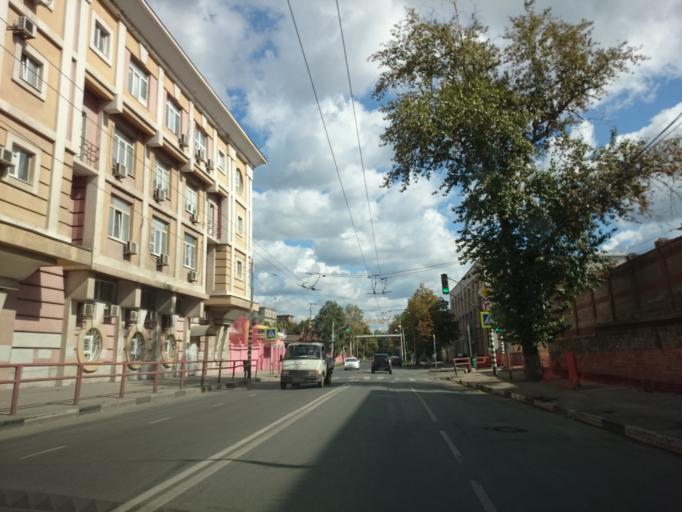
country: RU
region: Samara
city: Samara
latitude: 53.2021
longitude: 50.1025
